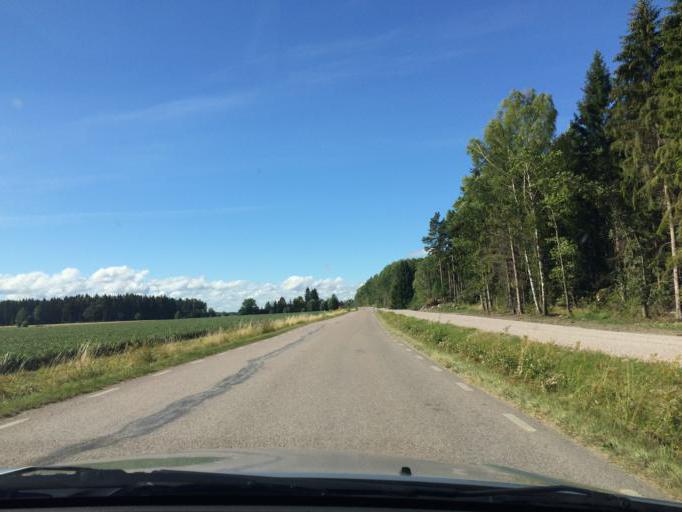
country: SE
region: Vaestmanland
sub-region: Vasteras
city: Vasteras
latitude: 59.5694
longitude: 16.4859
